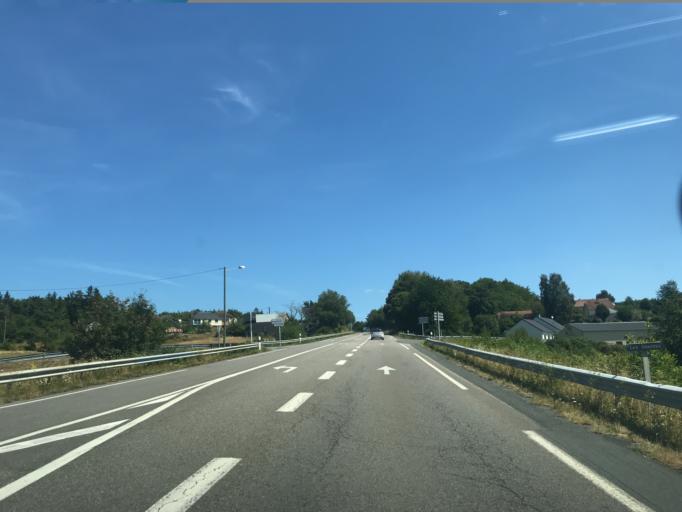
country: FR
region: Limousin
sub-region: Departement de la Correze
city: Correze
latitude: 45.3179
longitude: 1.8398
